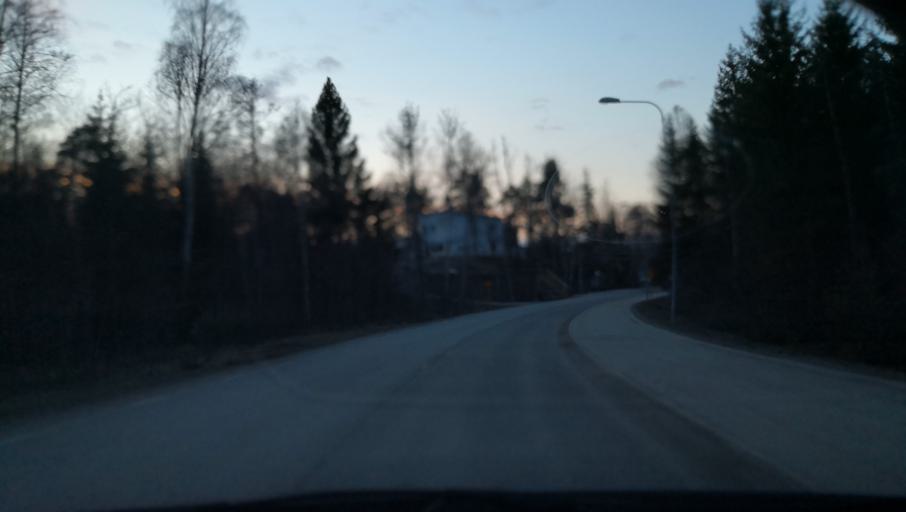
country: SE
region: Stockholm
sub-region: Nacka Kommun
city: Kummelnas
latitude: 59.3420
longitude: 18.2934
